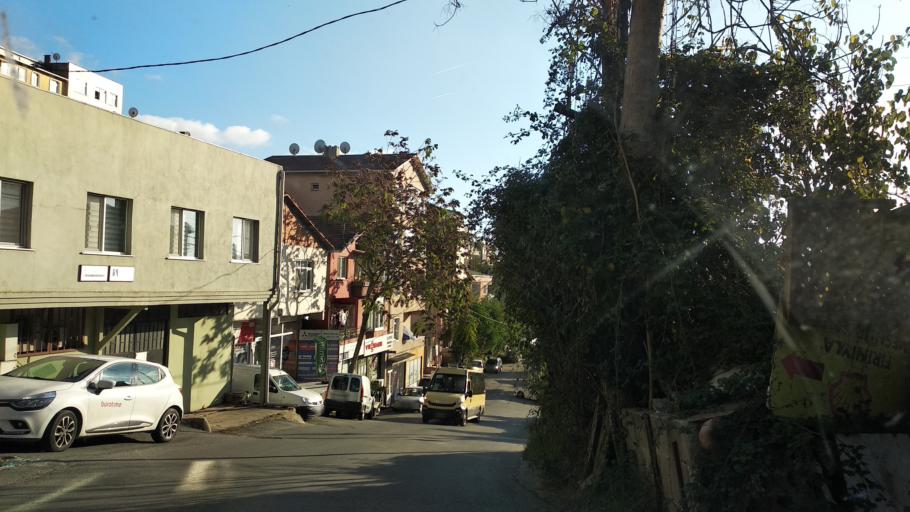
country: TR
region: Istanbul
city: Sisli
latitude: 41.1300
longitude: 29.0412
